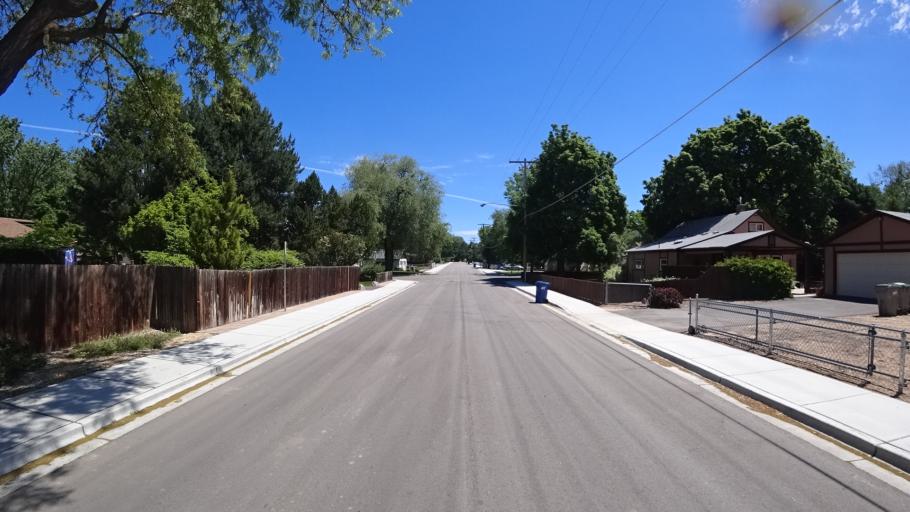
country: US
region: Idaho
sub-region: Ada County
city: Boise
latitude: 43.5826
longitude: -116.2217
